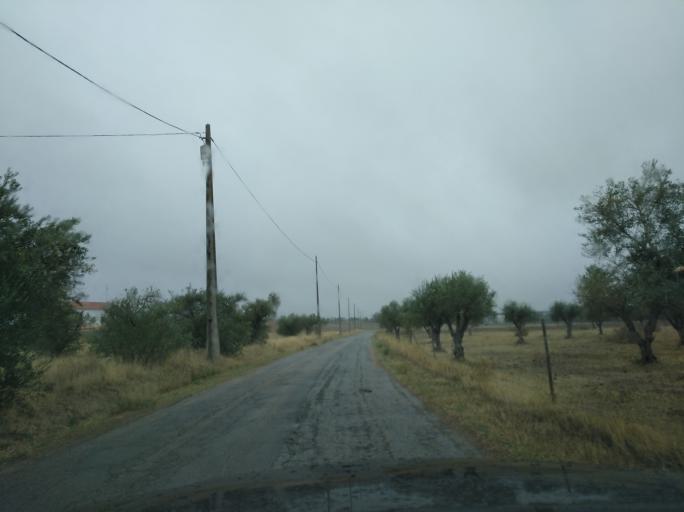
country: PT
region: Portalegre
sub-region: Campo Maior
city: Campo Maior
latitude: 38.9771
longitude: -7.0691
